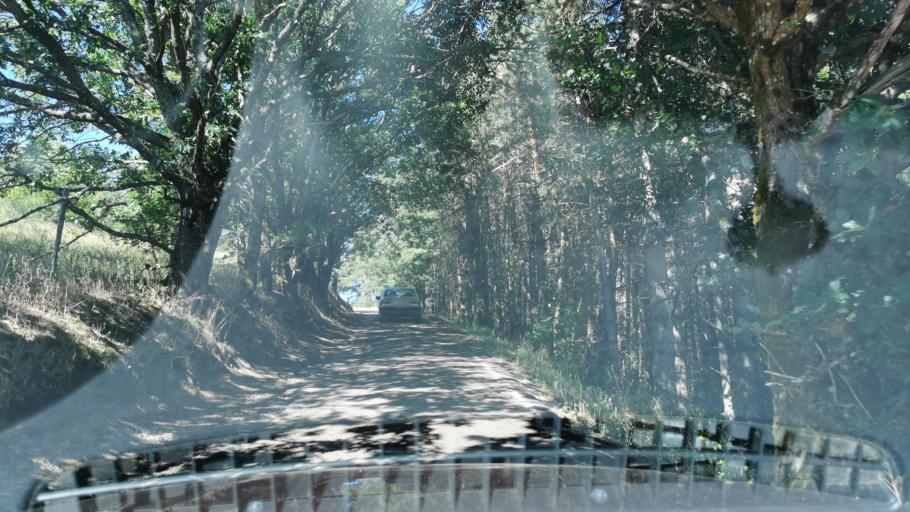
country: FR
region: Bourgogne
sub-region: Departement de Saone-et-Loire
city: Montcenis
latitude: 46.8001
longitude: 4.3918
